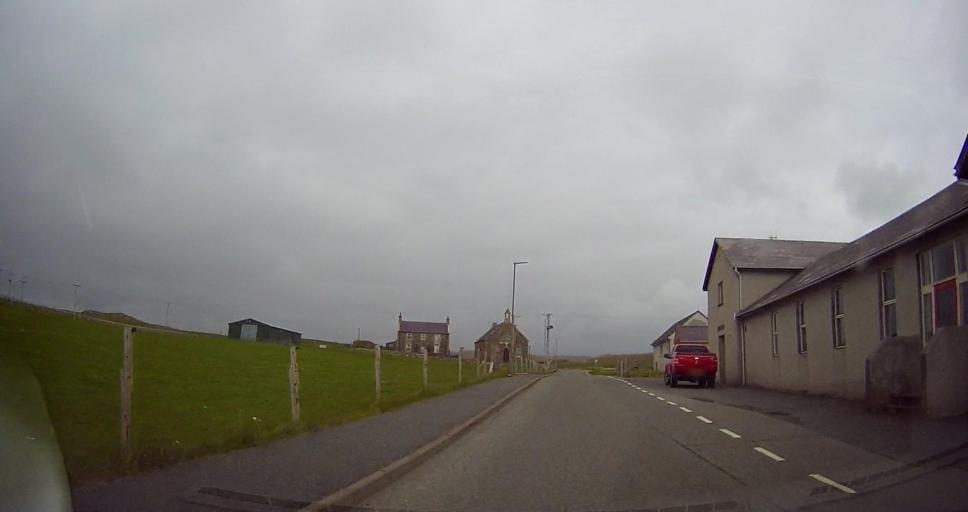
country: GB
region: Scotland
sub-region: Shetland Islands
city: Sandwick
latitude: 60.2292
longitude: -1.5637
